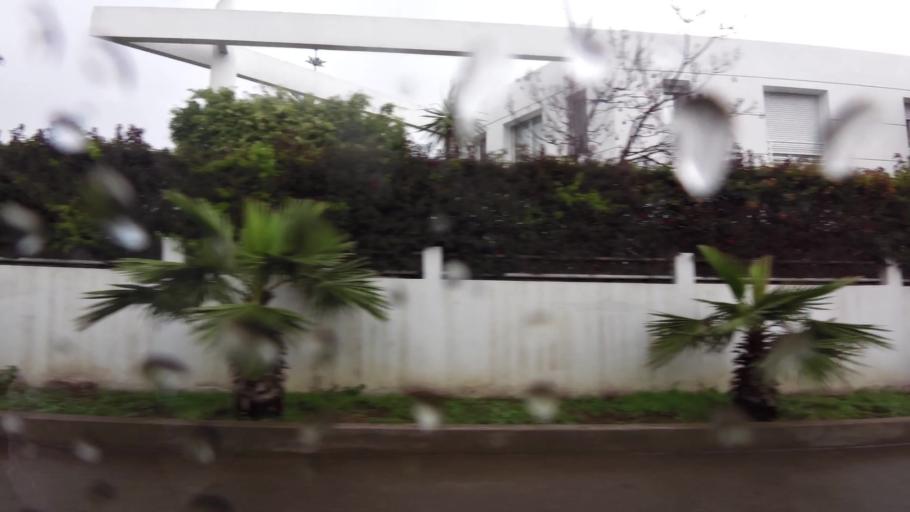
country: MA
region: Grand Casablanca
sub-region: Casablanca
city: Casablanca
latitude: 33.5413
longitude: -7.6645
